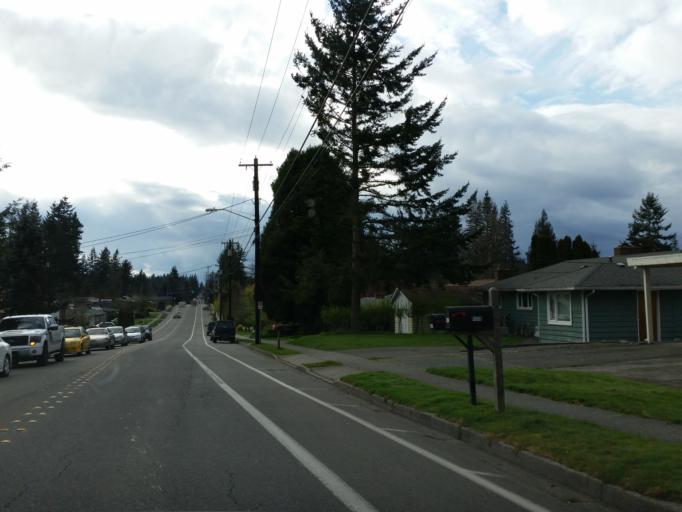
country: US
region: Washington
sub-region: Snohomish County
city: Alderwood Manor
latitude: 47.8283
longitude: -122.2985
